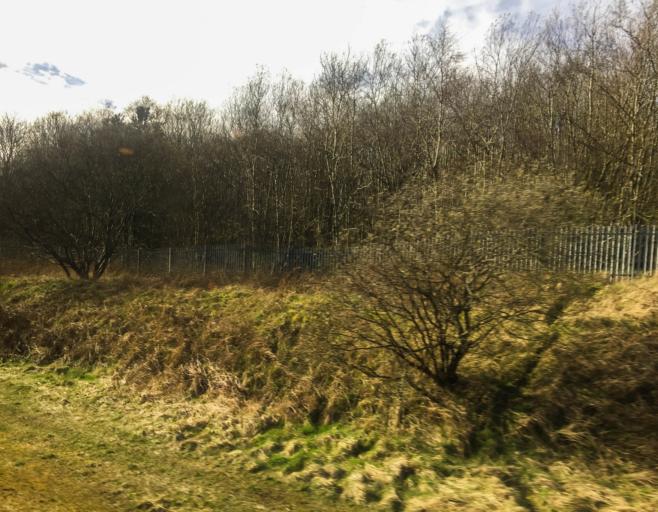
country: GB
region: Scotland
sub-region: North Lanarkshire
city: Stepps
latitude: 55.8832
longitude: -4.1840
